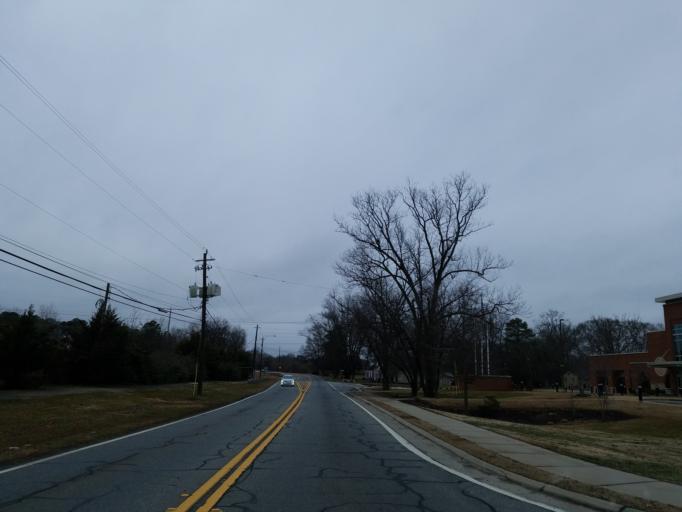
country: US
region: Georgia
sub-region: Bartow County
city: Cartersville
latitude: 34.1765
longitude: -84.8113
